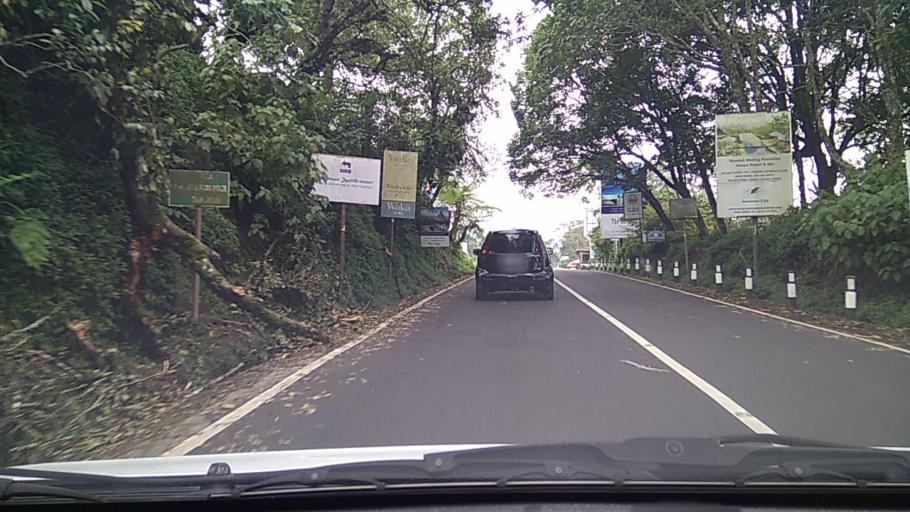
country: ID
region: Bali
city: Munduk
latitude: -8.2371
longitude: 115.1406
